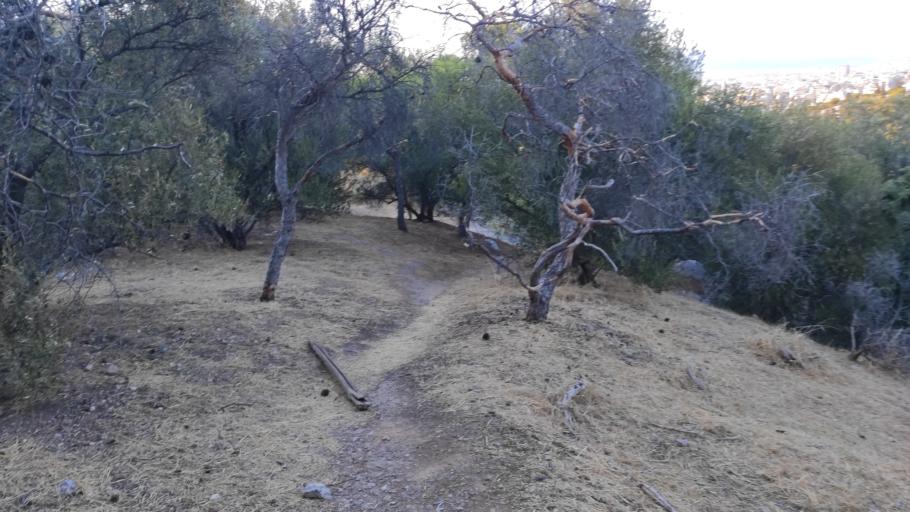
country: GR
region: Attica
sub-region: Nomarchia Athinas
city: Athens
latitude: 37.9689
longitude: 23.7208
